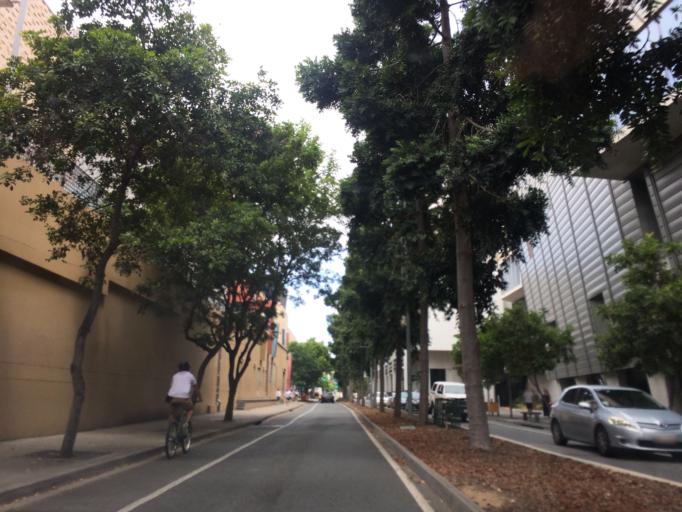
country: AU
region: Queensland
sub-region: Brisbane
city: South Brisbane
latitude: -27.4762
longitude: 153.0199
